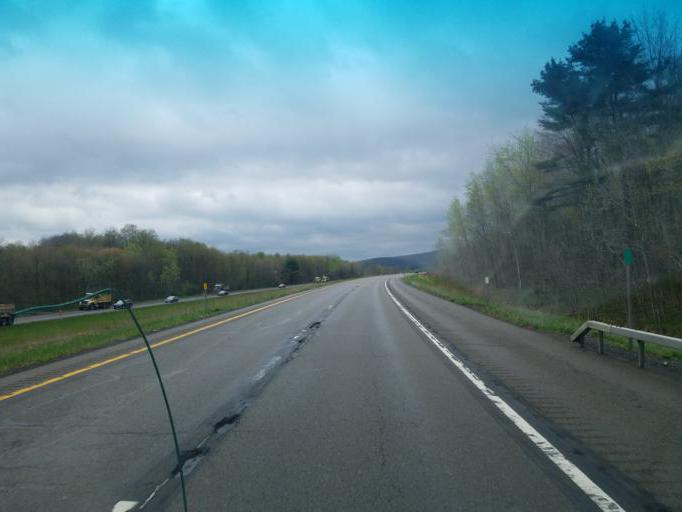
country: US
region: New York
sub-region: Cattaraugus County
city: Randolph
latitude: 42.1162
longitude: -78.9273
